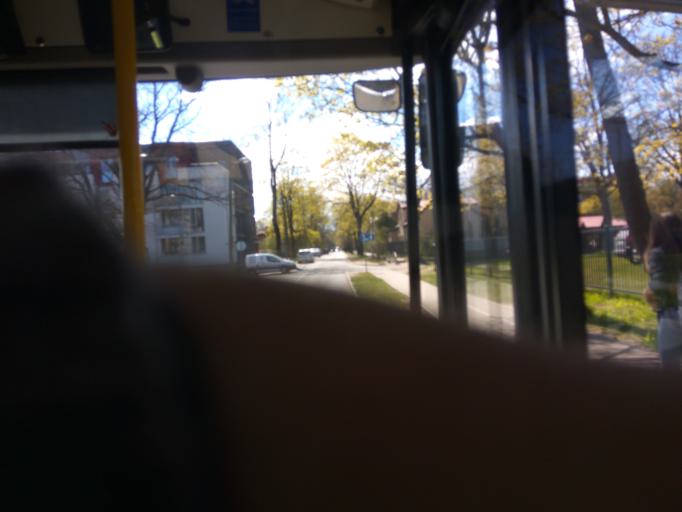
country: LV
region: Marupe
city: Marupe
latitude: 56.9378
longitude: 24.0402
